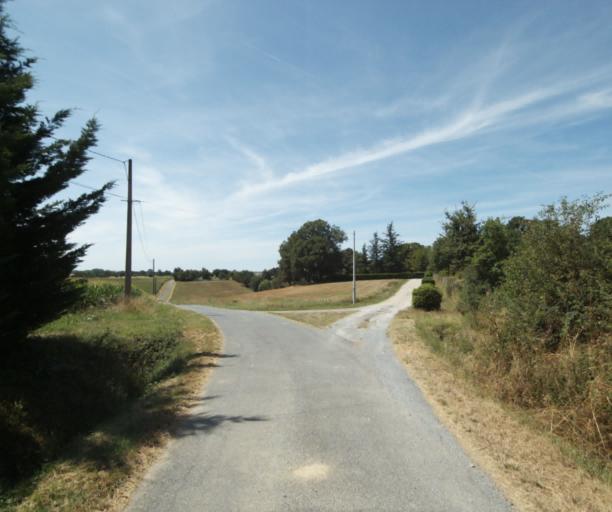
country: FR
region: Midi-Pyrenees
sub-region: Departement du Tarn
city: Puylaurens
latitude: 43.5359
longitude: 1.9987
